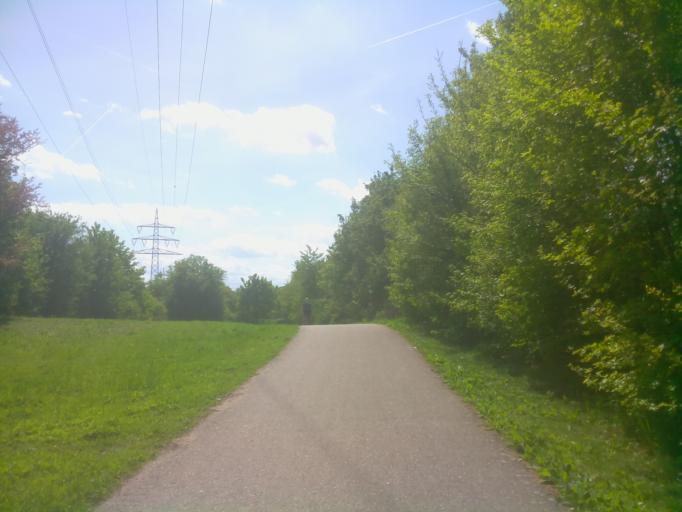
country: DE
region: Rheinland-Pfalz
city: Neuhofen
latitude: 49.4482
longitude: 8.4283
